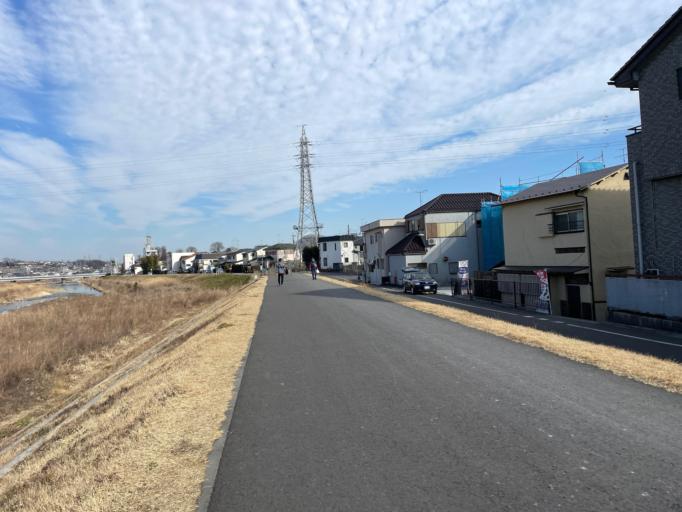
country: JP
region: Tokyo
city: Hachioji
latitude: 35.6654
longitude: 139.3253
